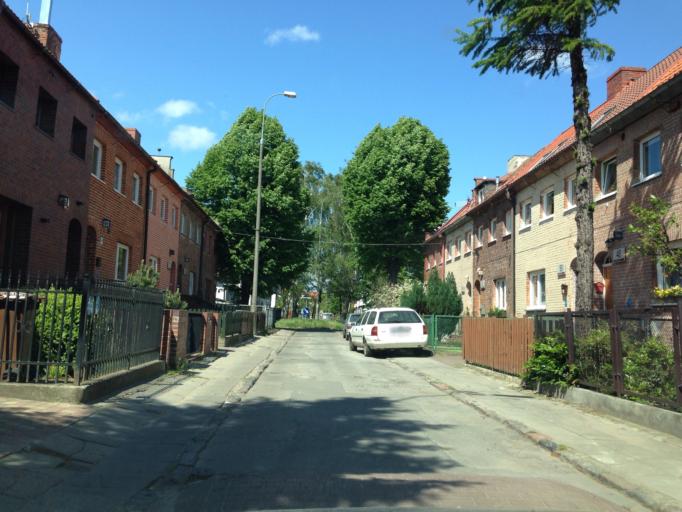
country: PL
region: Pomeranian Voivodeship
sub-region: Gdansk
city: Gdansk
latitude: 54.3851
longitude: 18.6203
